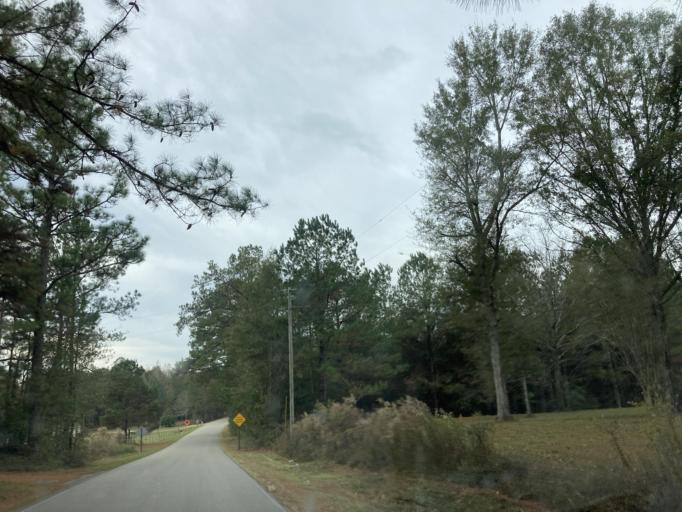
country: US
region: Mississippi
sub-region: Lamar County
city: Purvis
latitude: 31.1201
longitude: -89.4551
